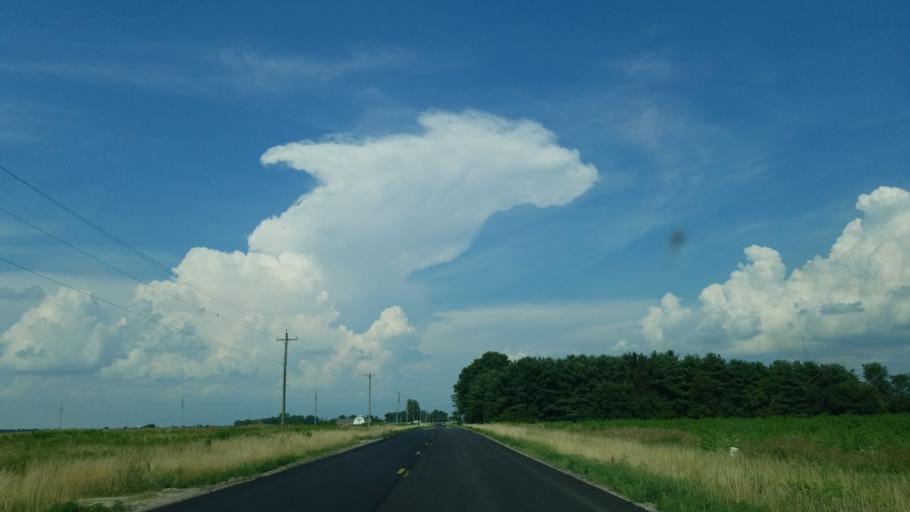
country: US
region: Ohio
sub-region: Delaware County
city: Delaware
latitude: 40.3200
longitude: -83.0252
